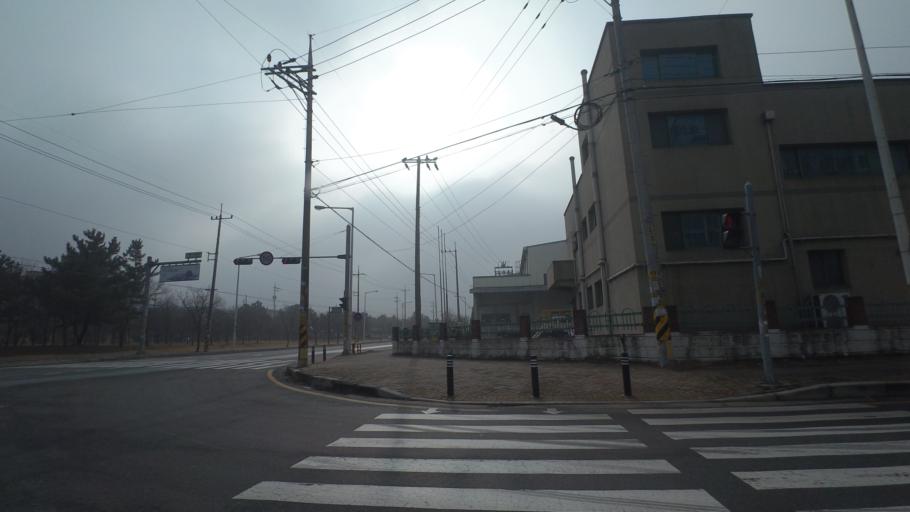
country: KR
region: Gyeonggi-do
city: Hwaseong-si
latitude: 36.9884
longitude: 126.8531
